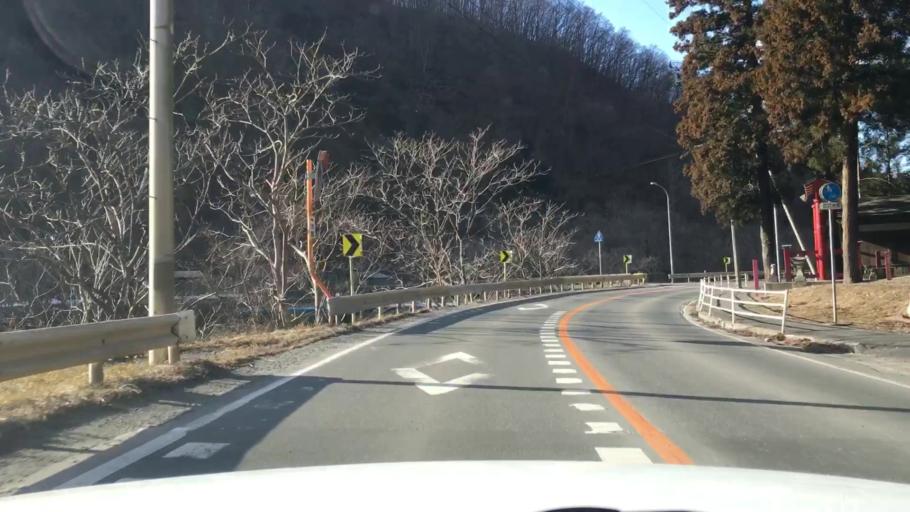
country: JP
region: Iwate
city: Miyako
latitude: 39.5903
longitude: 141.6664
